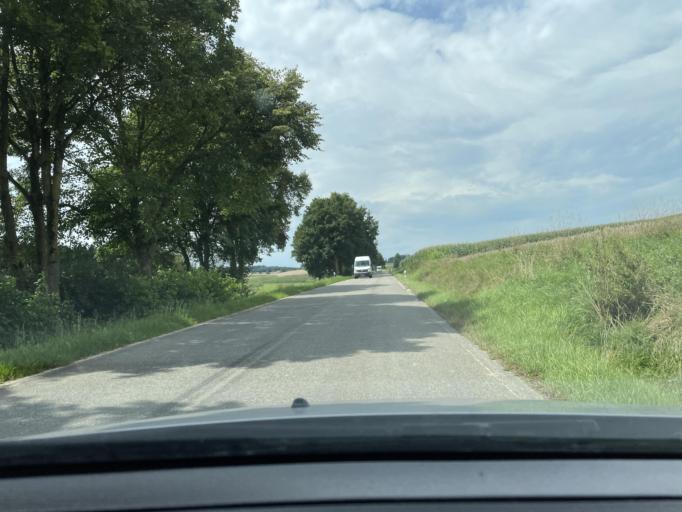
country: DE
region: Bavaria
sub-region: Lower Bavaria
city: Geisenhausen
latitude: 48.4408
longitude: 12.2668
